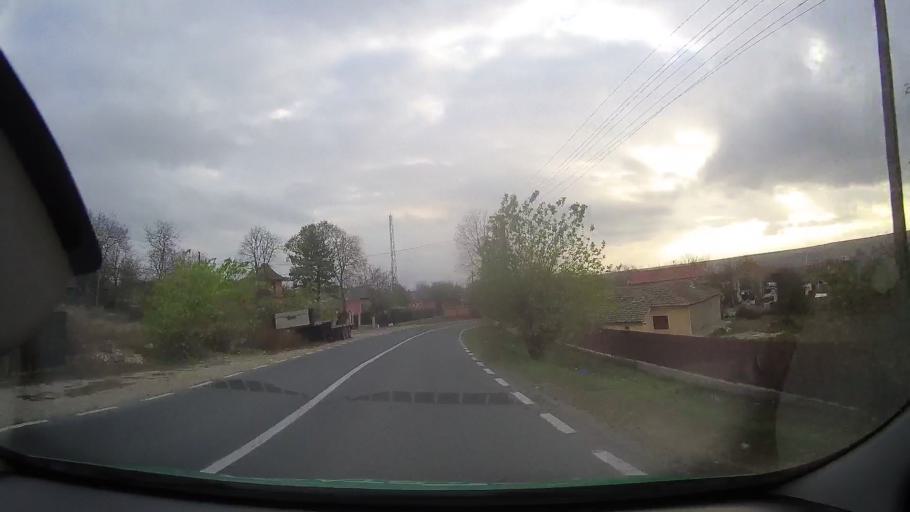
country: RO
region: Constanta
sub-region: Comuna Adamclisi
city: Adamclisi
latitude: 44.0865
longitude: 27.9608
